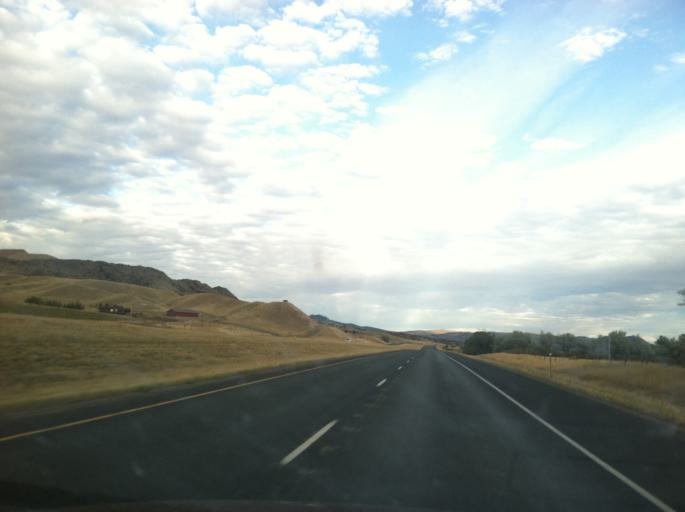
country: US
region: Montana
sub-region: Jefferson County
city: Whitehall
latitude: 45.8763
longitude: -112.0736
